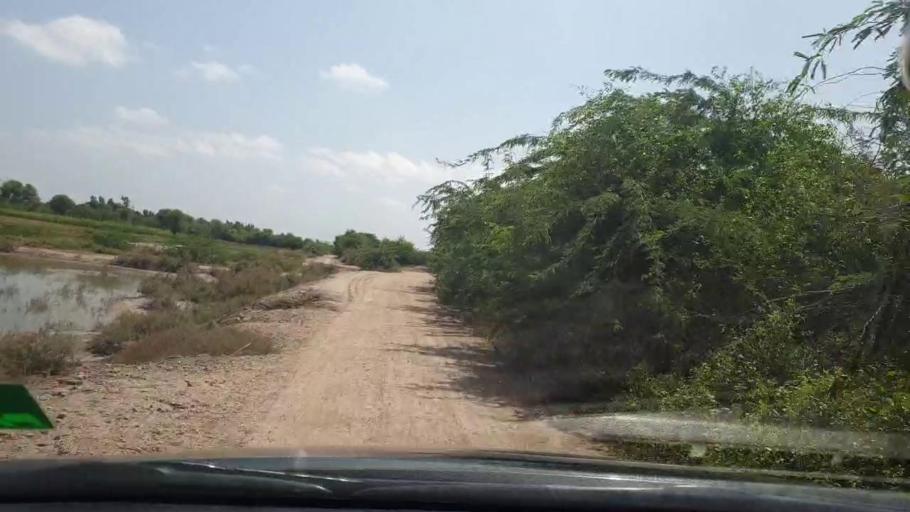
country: PK
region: Sindh
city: Tando Bago
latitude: 24.8530
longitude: 69.0910
